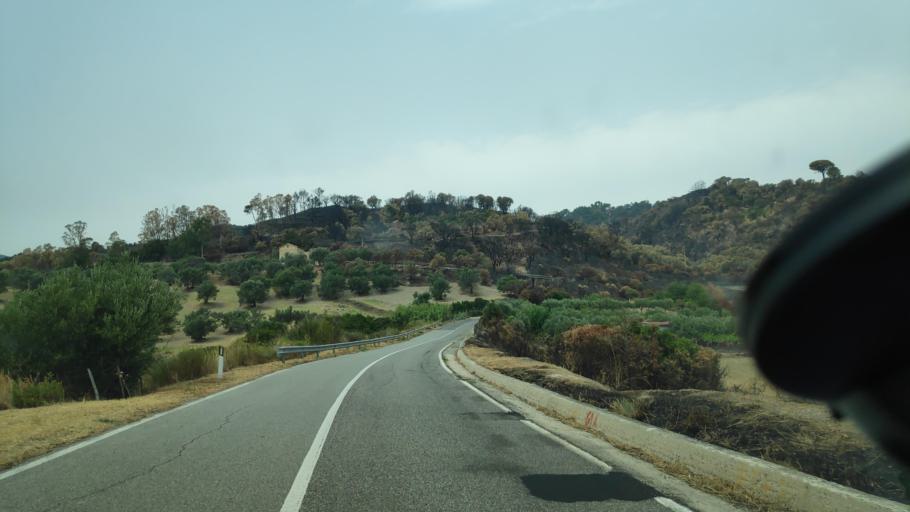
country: IT
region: Calabria
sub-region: Provincia di Catanzaro
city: Sant'Andrea Apostolo dello Ionio
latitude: 38.6412
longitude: 16.5242
